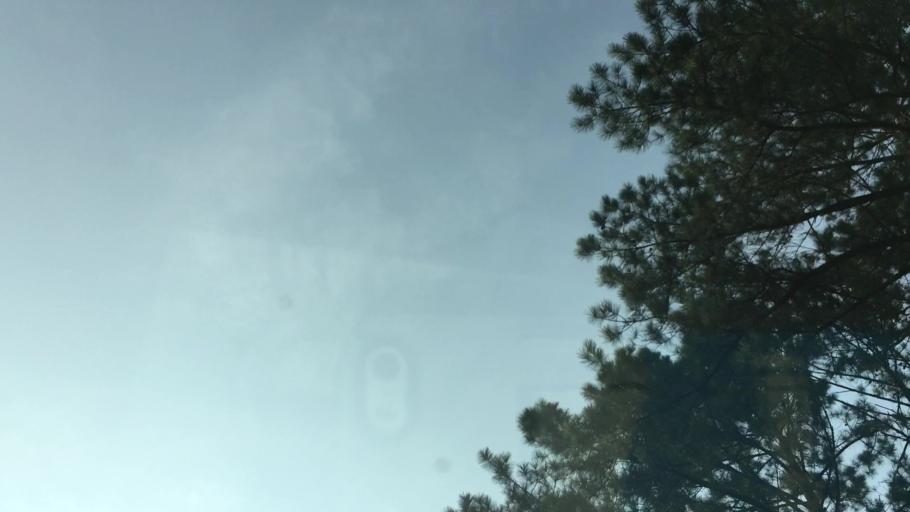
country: US
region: Alabama
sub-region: Tuscaloosa County
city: Lake View
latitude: 33.2202
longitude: -87.0045
